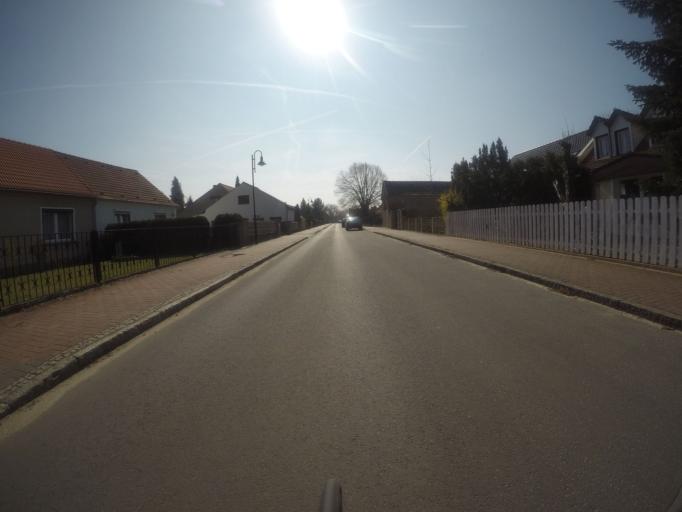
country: DE
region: Brandenburg
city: Erkner
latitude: 52.3916
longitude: 13.7128
